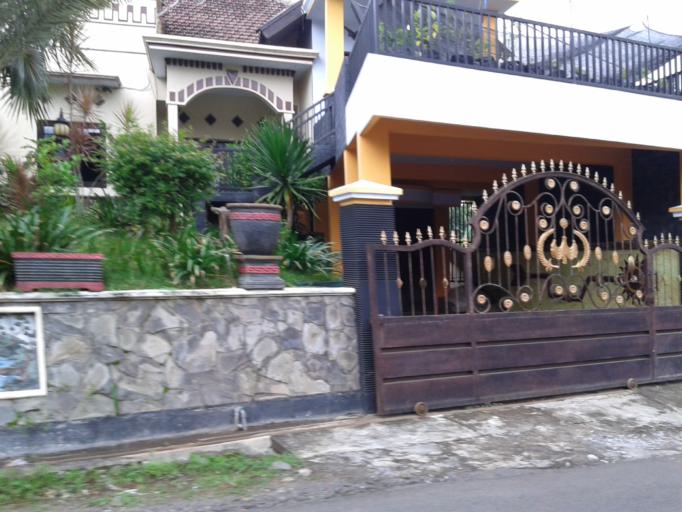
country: ID
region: East Java
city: Singosari
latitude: -7.9299
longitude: 112.6669
